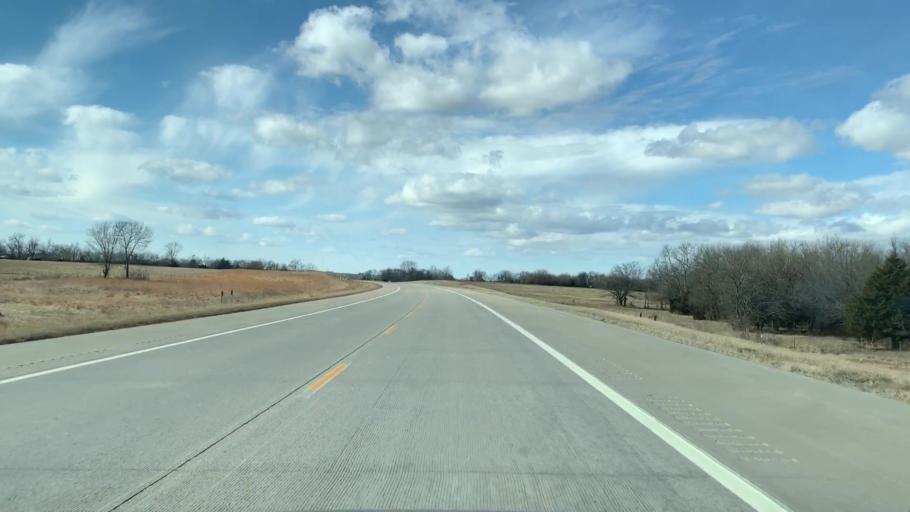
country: US
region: Kansas
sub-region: Labette County
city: Parsons
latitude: 37.3591
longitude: -95.2204
